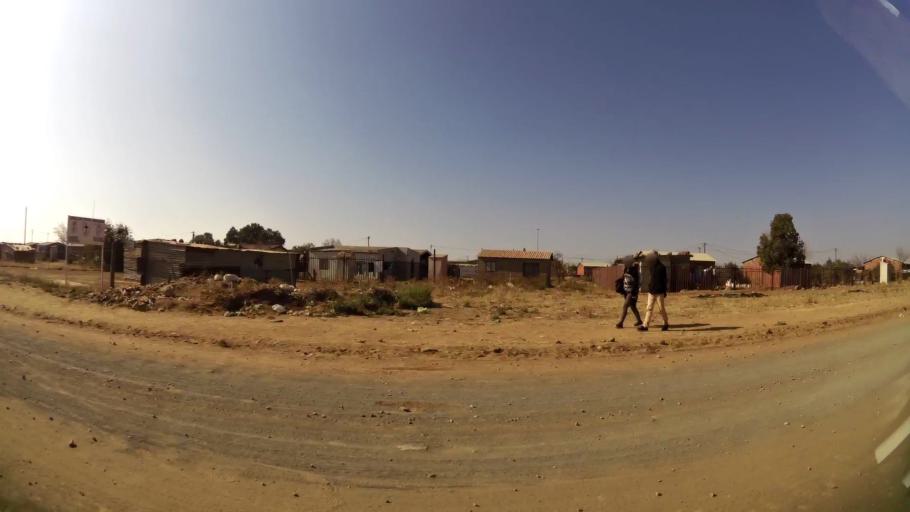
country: ZA
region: Orange Free State
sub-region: Mangaung Metropolitan Municipality
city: Bloemfontein
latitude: -29.1837
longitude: 26.2851
